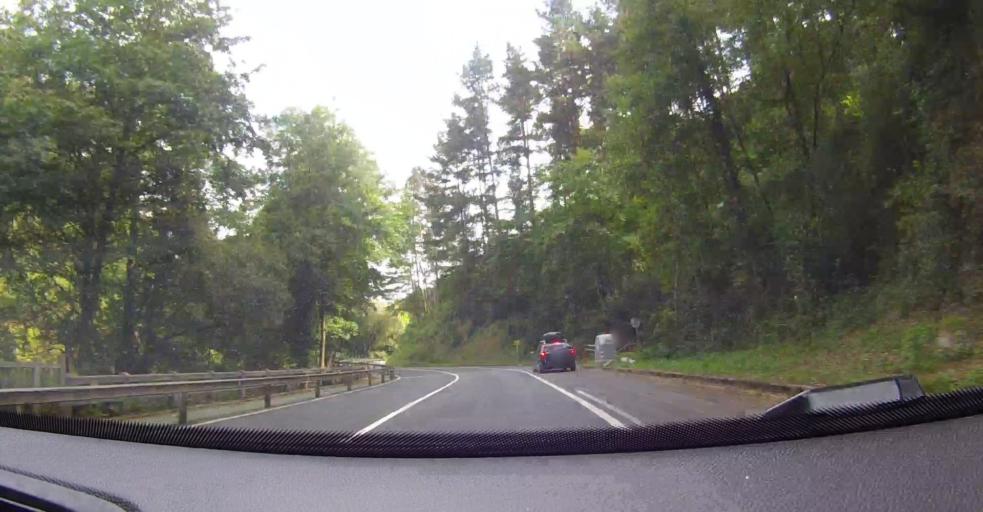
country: ES
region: Basque Country
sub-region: Bizkaia
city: Elantxobe
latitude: 43.4008
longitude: -2.6474
